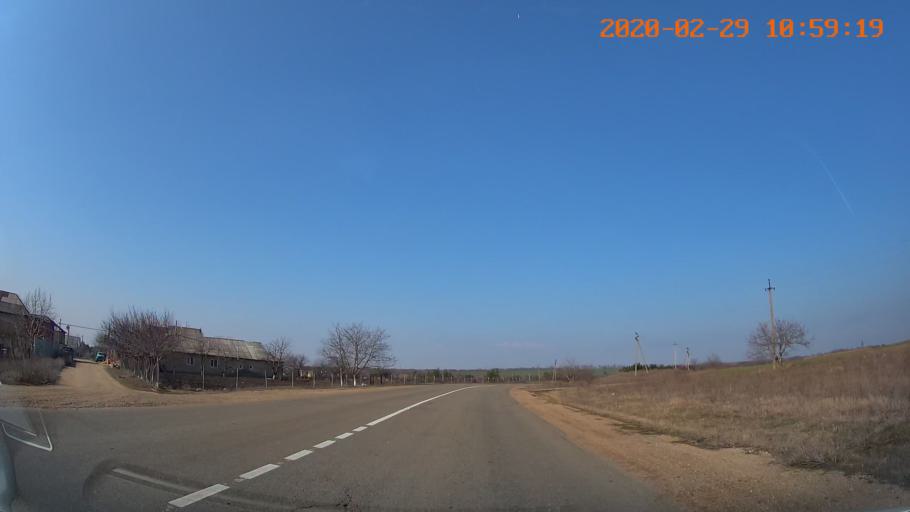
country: MD
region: Telenesti
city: Grigoriopol
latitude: 47.1645
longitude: 29.2937
